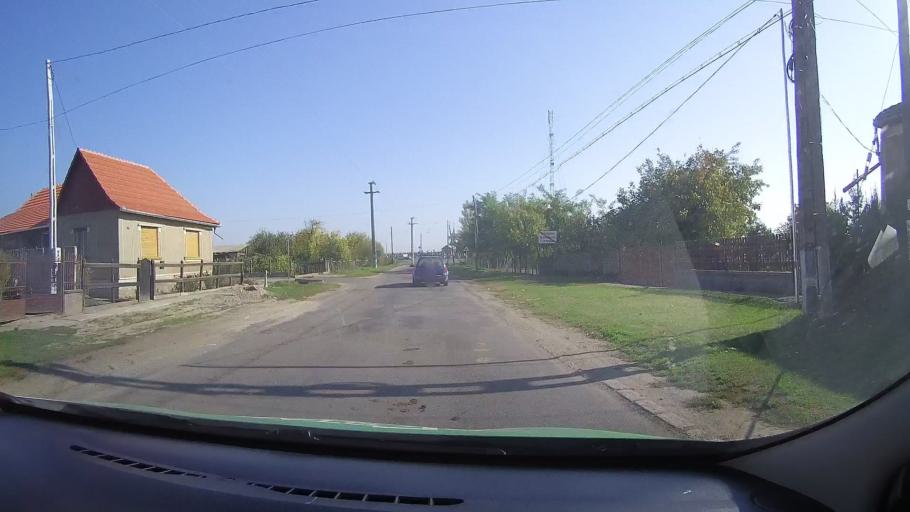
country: RO
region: Satu Mare
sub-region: Comuna Sanislau
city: Sanislau
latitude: 47.6423
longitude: 22.3325
